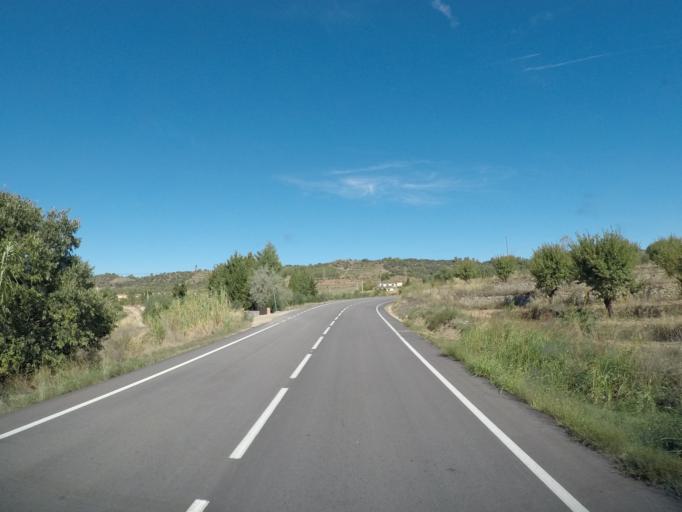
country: ES
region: Catalonia
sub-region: Provincia de Tarragona
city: Falset
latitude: 41.1563
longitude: 0.8150
